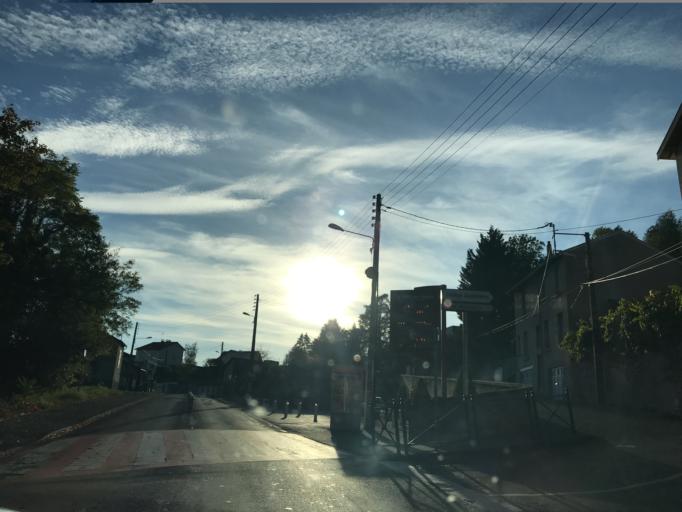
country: FR
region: Auvergne
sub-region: Departement du Puy-de-Dome
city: Thiers
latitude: 45.8619
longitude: 3.5394
